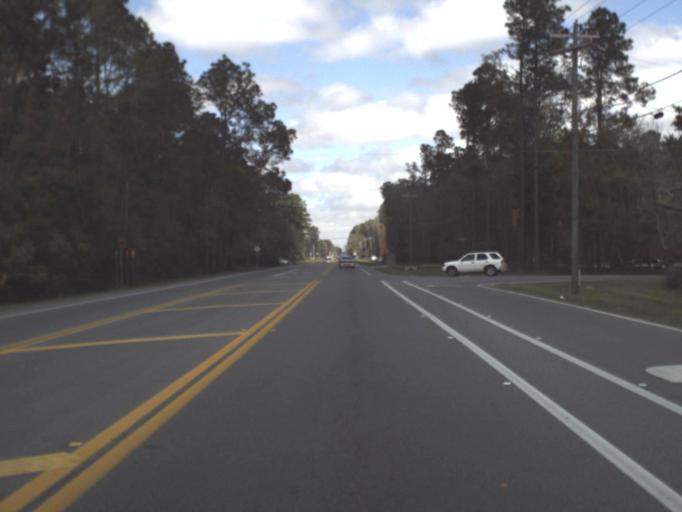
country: US
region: Florida
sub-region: Wakulla County
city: Crawfordville
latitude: 30.2231
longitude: -84.3624
